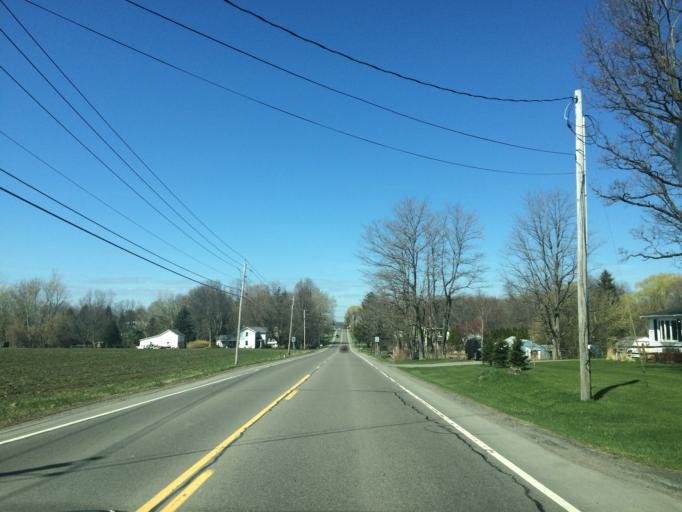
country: US
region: New York
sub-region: Wayne County
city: Macedon
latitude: 43.0942
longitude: -77.3144
